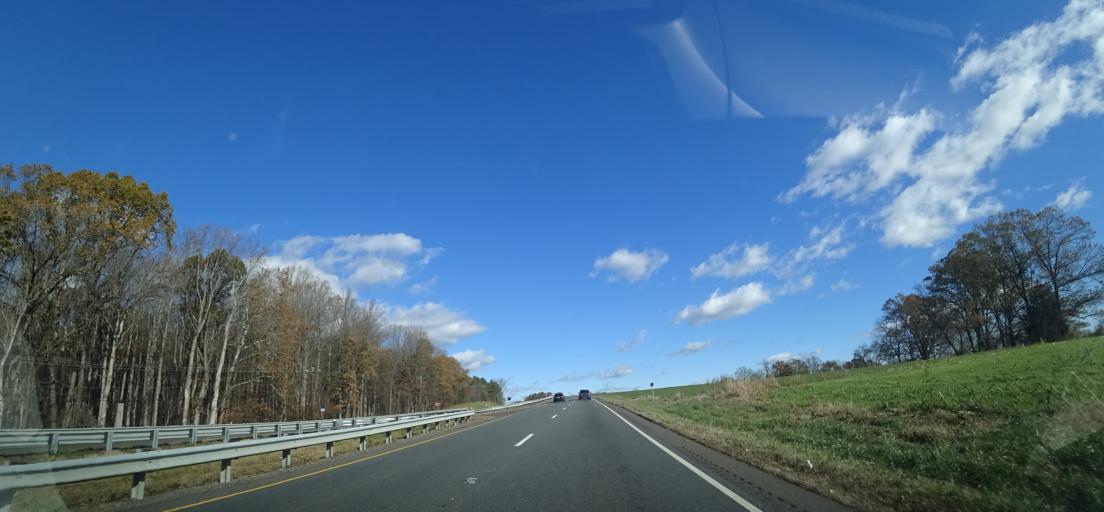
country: US
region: Virginia
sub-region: Greene County
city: Ruckersville
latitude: 38.2864
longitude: -78.3358
